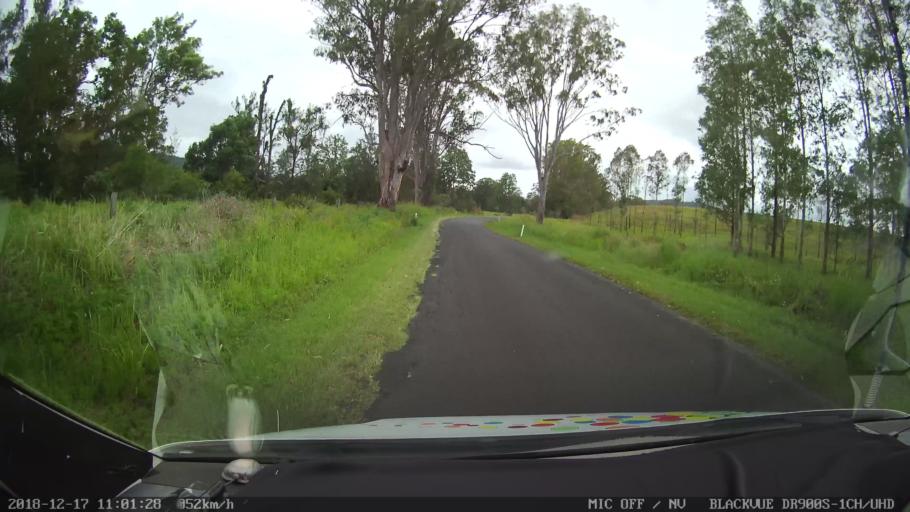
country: AU
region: New South Wales
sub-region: Richmond Valley
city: Casino
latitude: -28.8154
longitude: 152.6256
